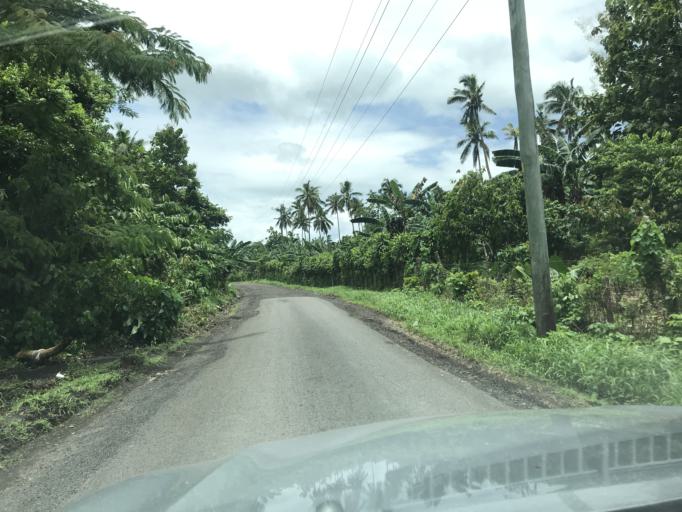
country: WS
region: Tuamasaga
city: Afenga
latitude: -13.8185
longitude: -171.8849
